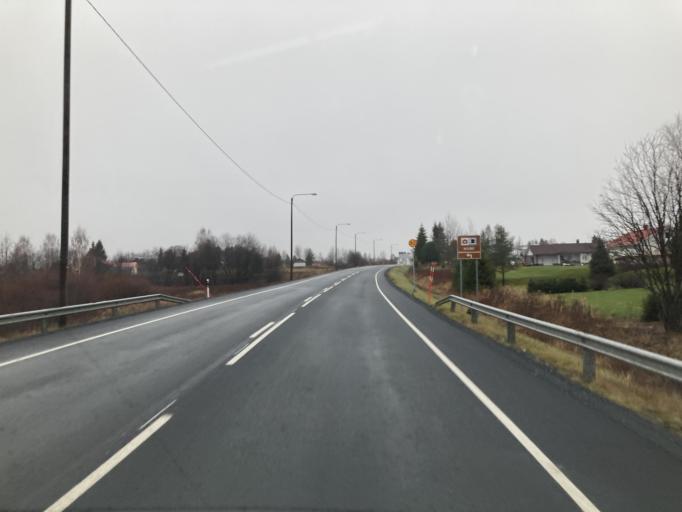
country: FI
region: Lapland
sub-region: Torniolaakso
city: Ylitornio
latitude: 66.3195
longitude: 23.6665
